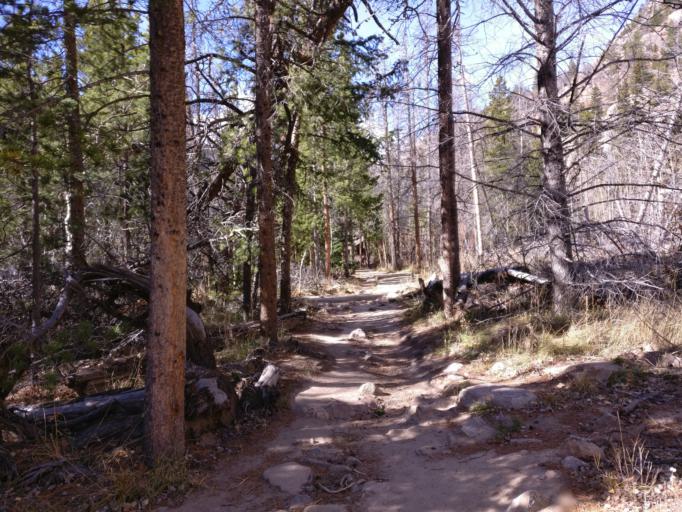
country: US
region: Colorado
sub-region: Larimer County
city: Estes Park
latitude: 40.3506
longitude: -105.6509
